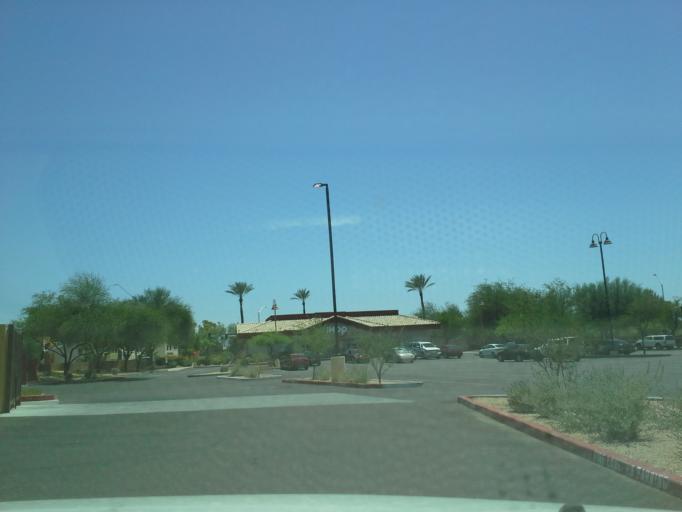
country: US
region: Arizona
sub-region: Maricopa County
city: Scottsdale
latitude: 33.5765
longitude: -111.8864
